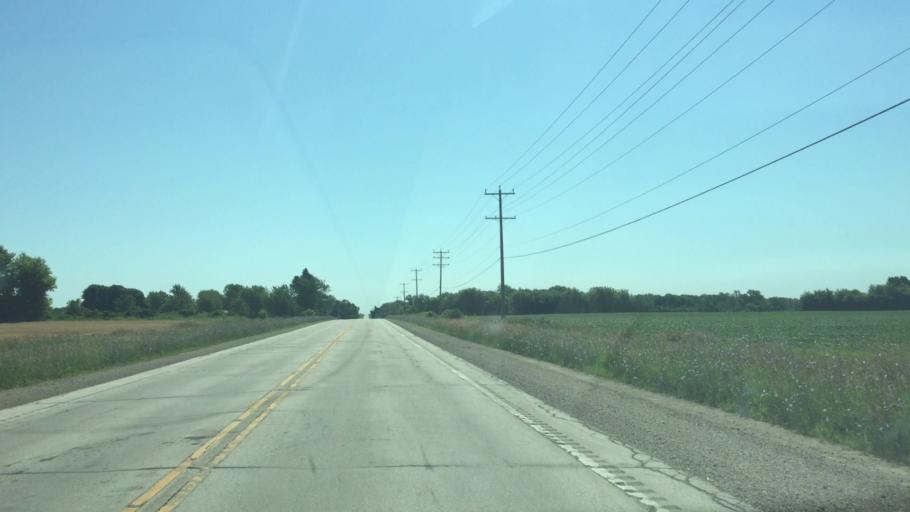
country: US
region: Wisconsin
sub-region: Calumet County
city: Sherwood
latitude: 44.1410
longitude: -88.2613
